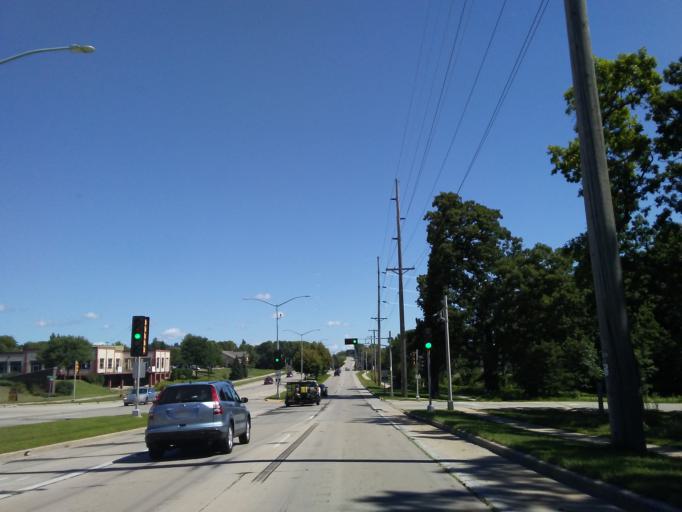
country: US
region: Wisconsin
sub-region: Dane County
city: Madison
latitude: 43.0187
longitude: -89.4197
